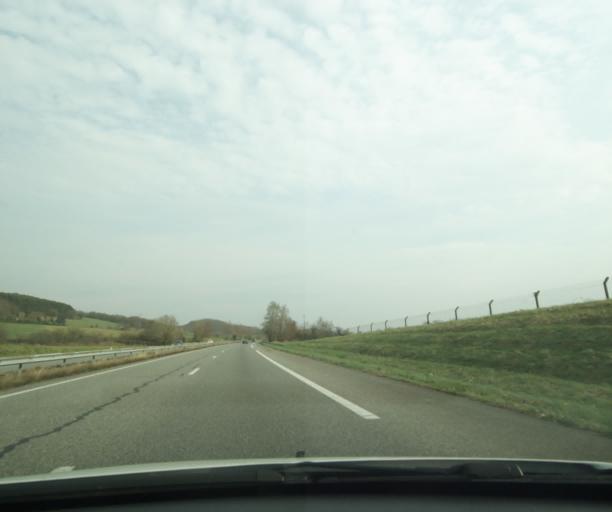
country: FR
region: Aquitaine
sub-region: Departement des Pyrenees-Atlantiques
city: Denguin
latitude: 43.3837
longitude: -0.5084
